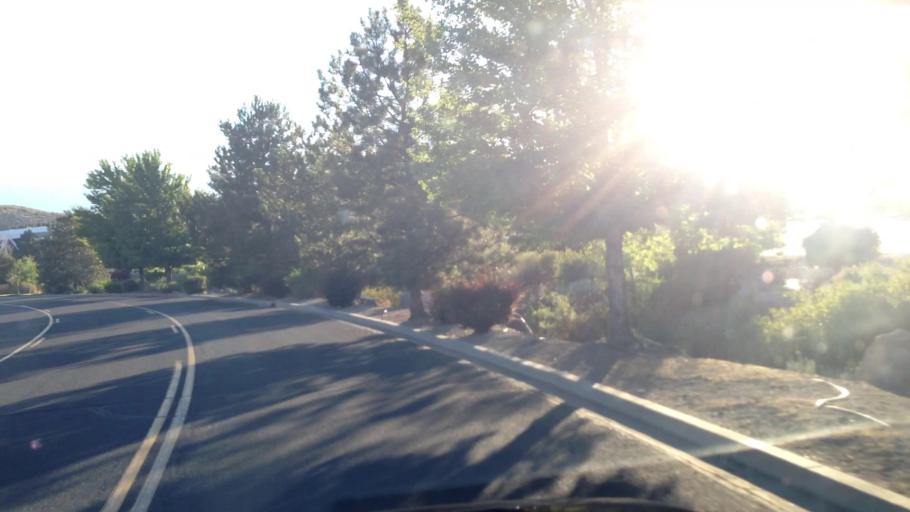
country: US
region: Nevada
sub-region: Washoe County
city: Sparks
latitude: 39.4515
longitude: -119.7591
